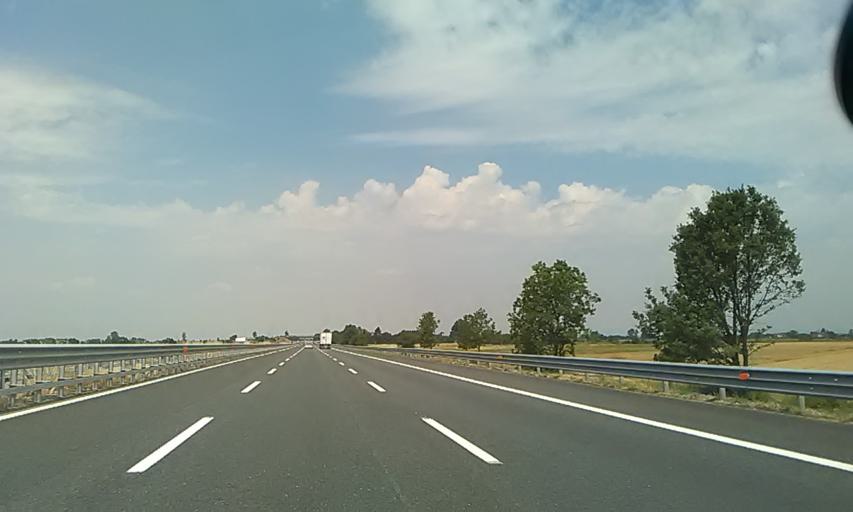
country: IT
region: Piedmont
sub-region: Provincia di Alessandria
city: Predosa
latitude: 44.7730
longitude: 8.6286
